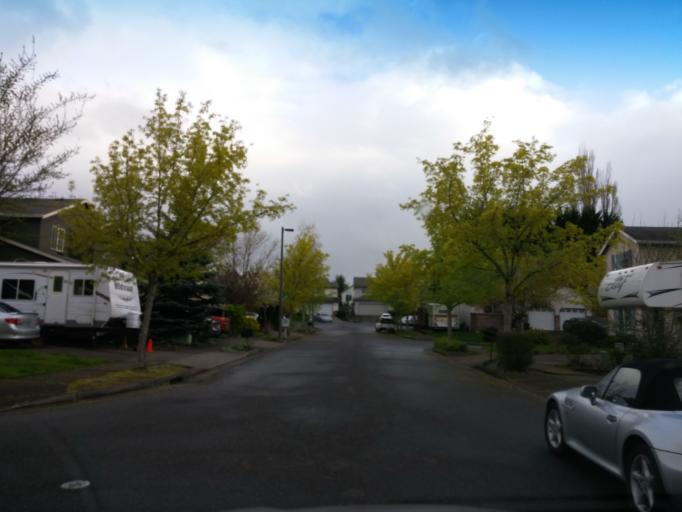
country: US
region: Oregon
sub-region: Washington County
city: Oak Hills
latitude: 45.5188
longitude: -122.8533
